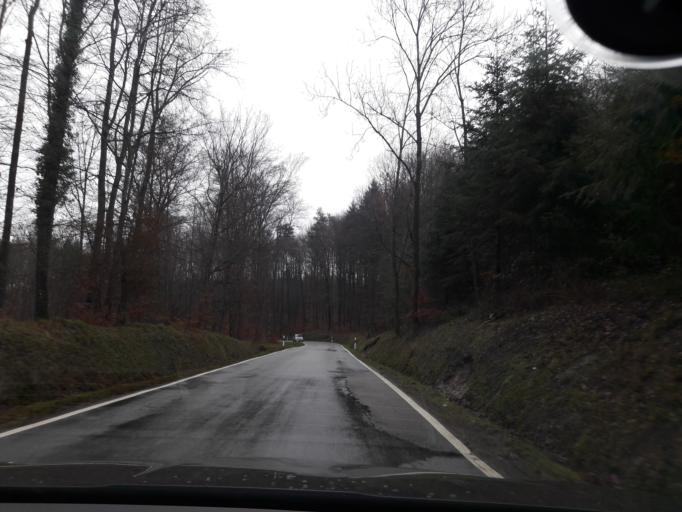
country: DE
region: Baden-Wuerttemberg
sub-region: Regierungsbezirk Stuttgart
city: Lowenstein
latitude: 49.0793
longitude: 9.3998
